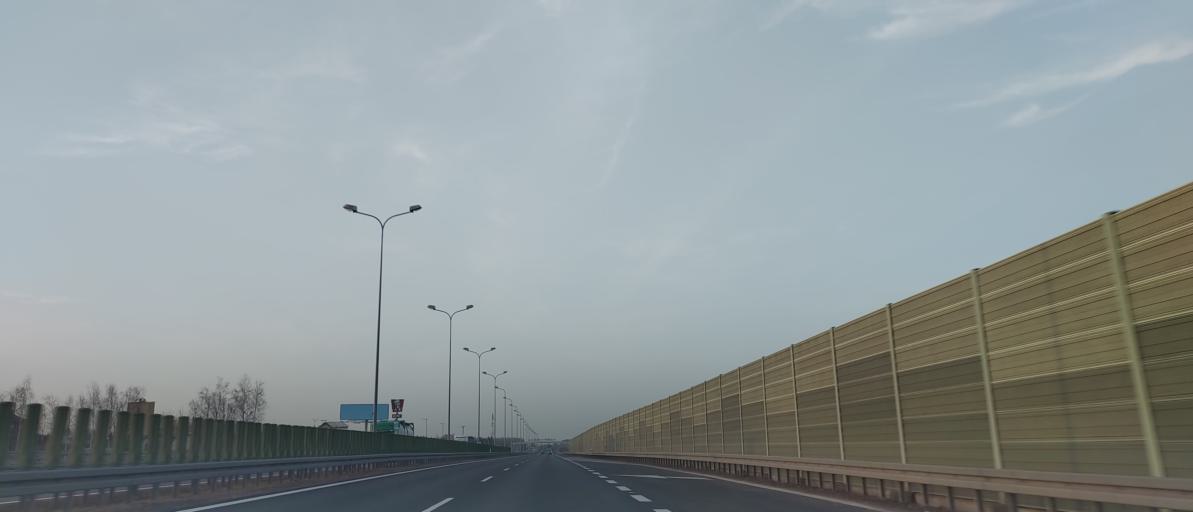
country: PL
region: Masovian Voivodeship
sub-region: Powiat bialobrzeski
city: Promna
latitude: 51.6955
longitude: 20.9334
